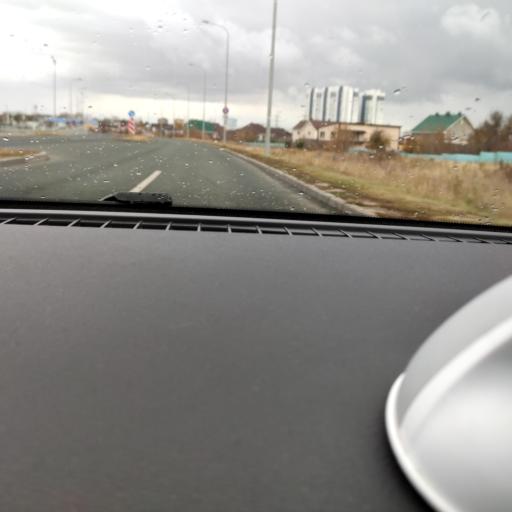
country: RU
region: Samara
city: Samara
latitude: 53.2733
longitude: 50.2323
